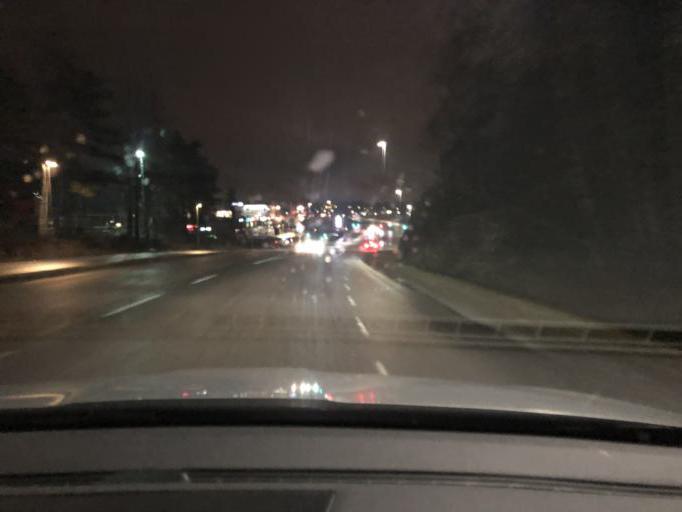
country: SE
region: Stockholm
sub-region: Jarfalla Kommun
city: Jakobsberg
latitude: 59.4060
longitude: 17.8364
